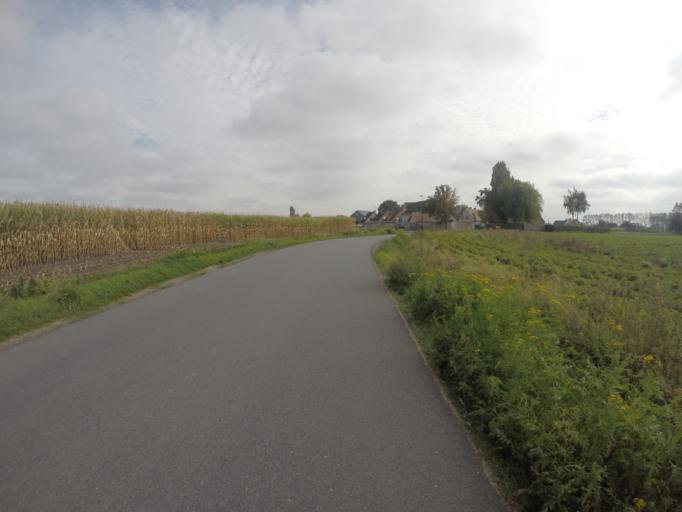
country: BE
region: Flanders
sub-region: Provincie Oost-Vlaanderen
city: Aalter
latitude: 51.0730
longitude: 3.4319
